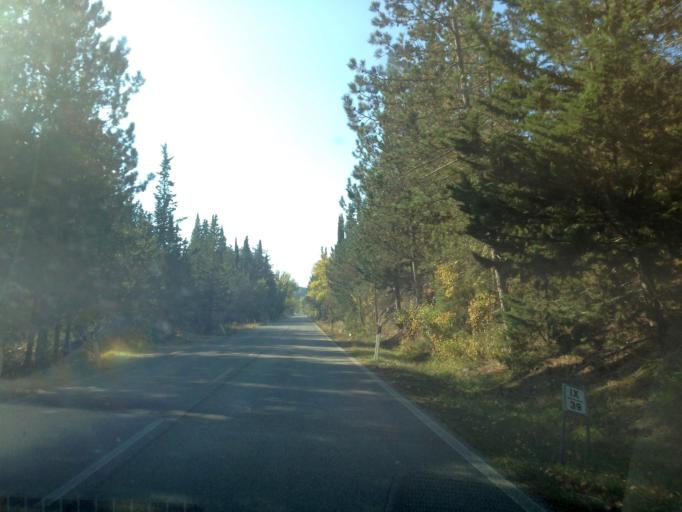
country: IT
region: Tuscany
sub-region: Provincia di Siena
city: Castellina in Chianti
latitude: 43.4870
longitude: 11.2992
